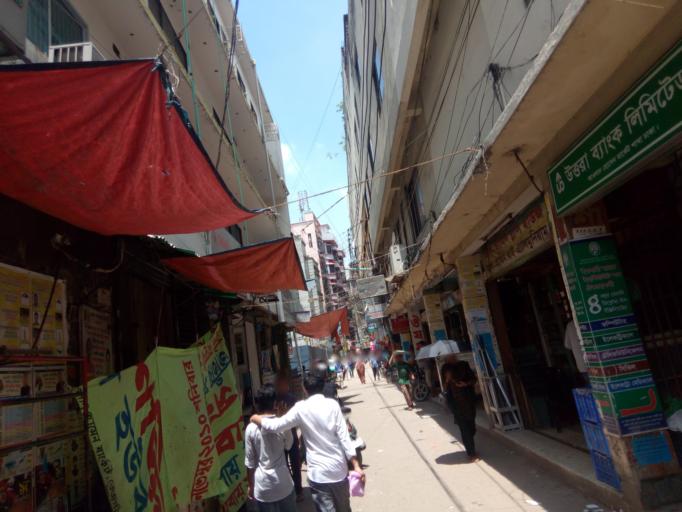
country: BD
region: Dhaka
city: Azimpur
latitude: 23.7630
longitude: 90.3894
